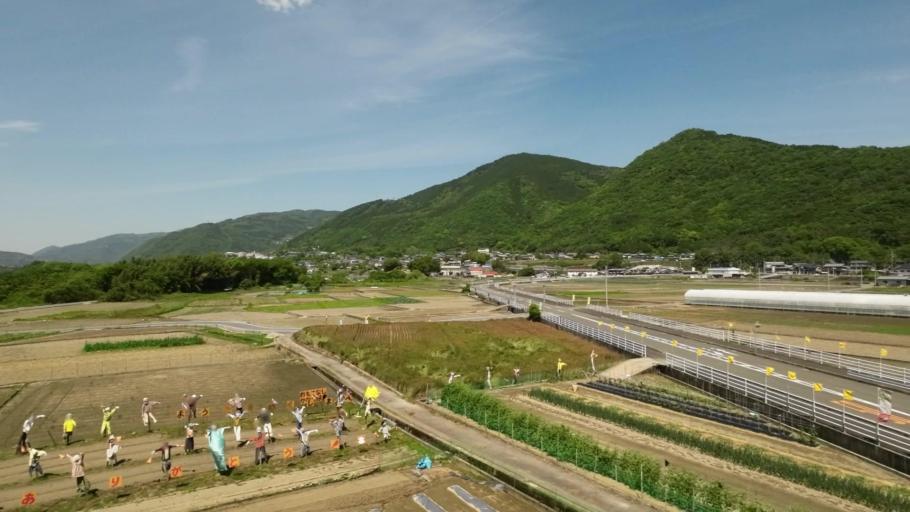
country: JP
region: Tokushima
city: Ikedacho
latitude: 34.0379
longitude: 133.8651
